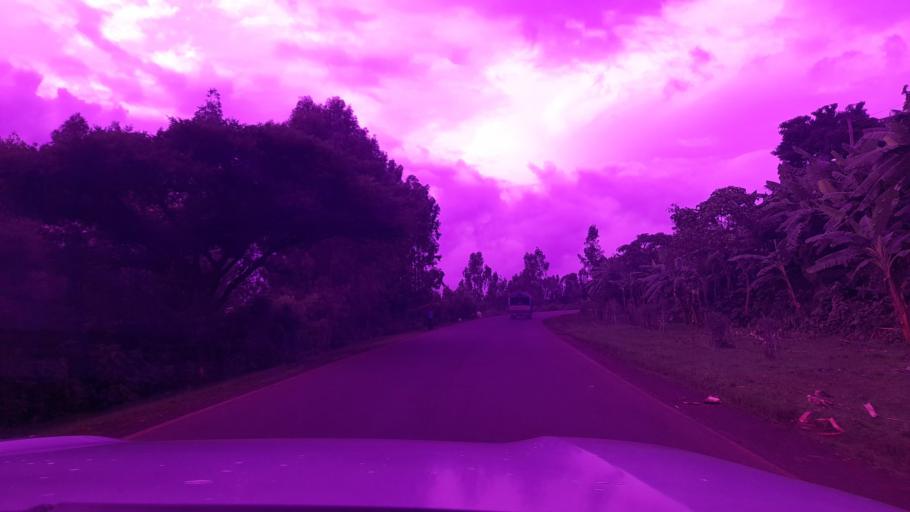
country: ET
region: Oromiya
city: Jima
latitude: 7.9025
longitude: 37.3900
